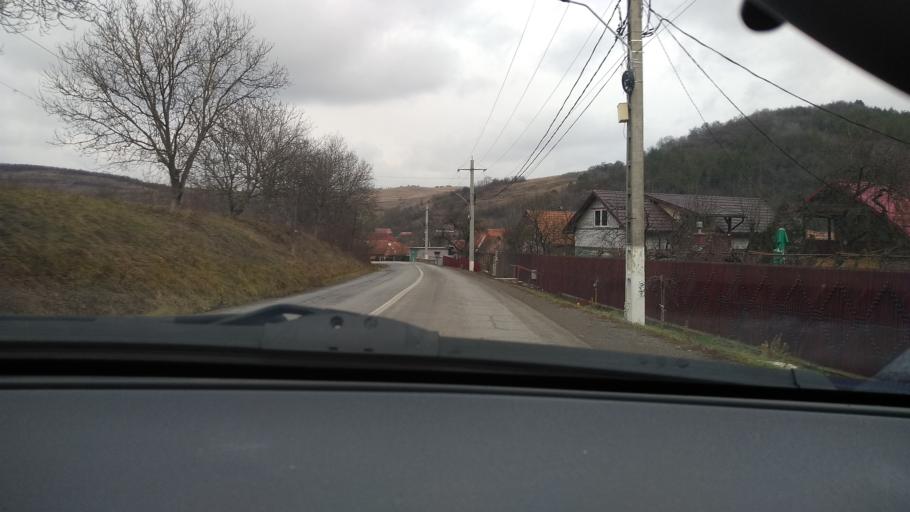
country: RO
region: Mures
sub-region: Comuna Pasareni
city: Pasareni
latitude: 46.5404
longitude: 24.6941
